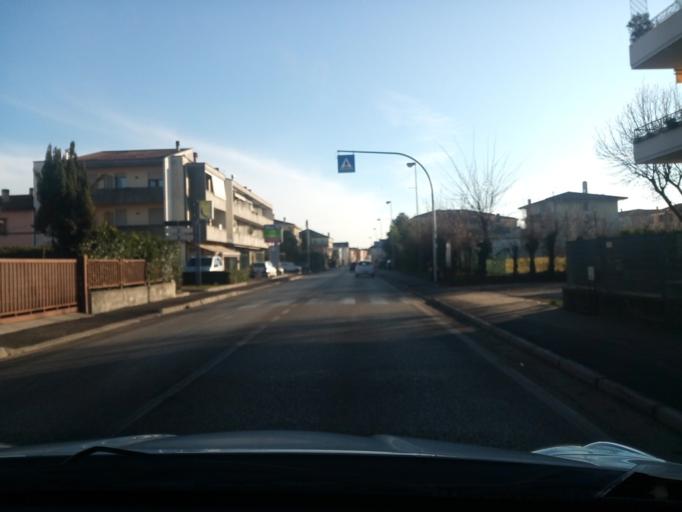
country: IT
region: Veneto
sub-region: Provincia di Vicenza
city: Villaverla
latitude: 45.6582
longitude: 11.4930
